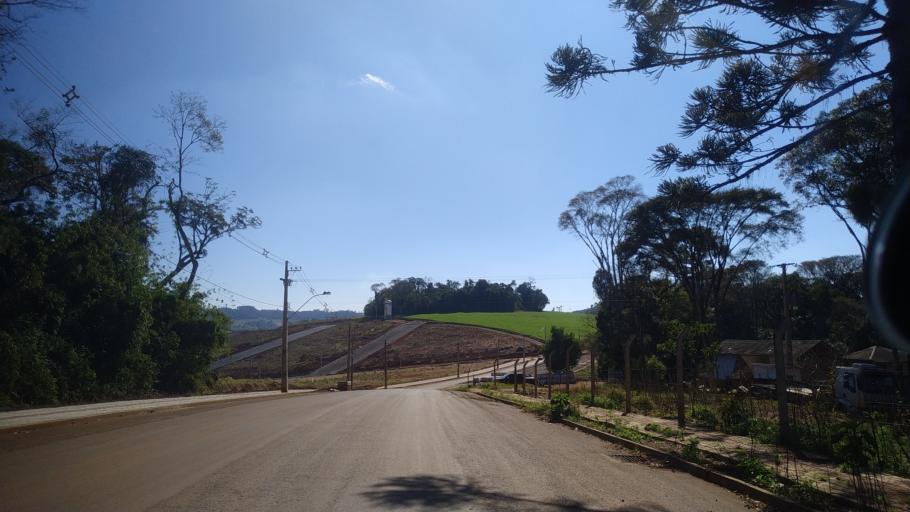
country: BR
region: Santa Catarina
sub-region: Chapeco
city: Chapeco
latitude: -27.0870
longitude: -52.6921
